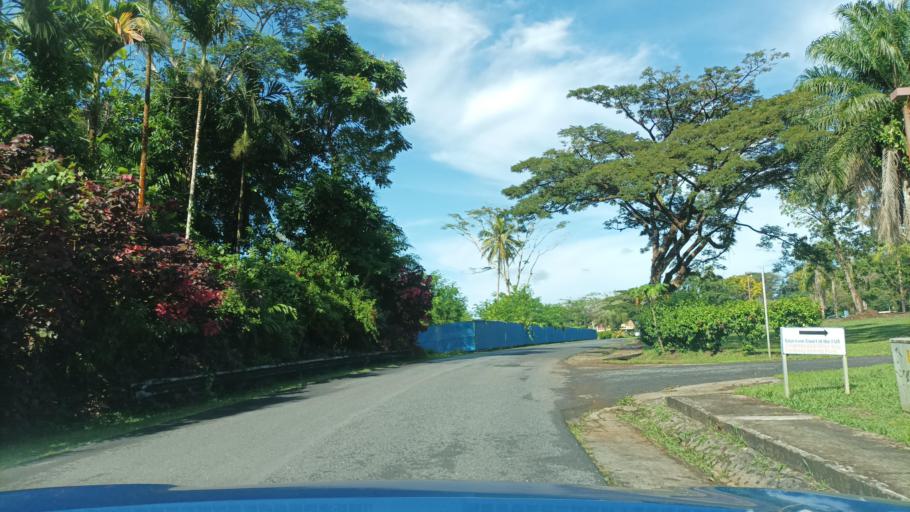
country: FM
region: Pohnpei
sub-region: Sokehs Municipality
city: Palikir - National Government Center
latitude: 6.9246
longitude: 158.1630
